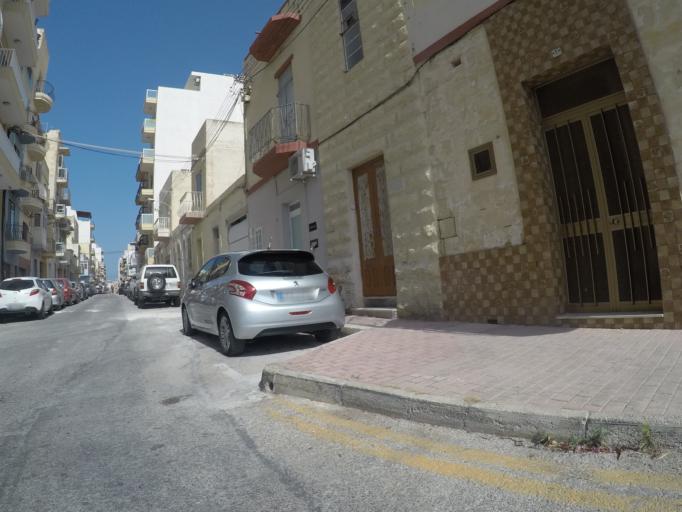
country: MT
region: Saint Paul's Bay
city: San Pawl il-Bahar
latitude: 35.9513
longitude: 14.4090
